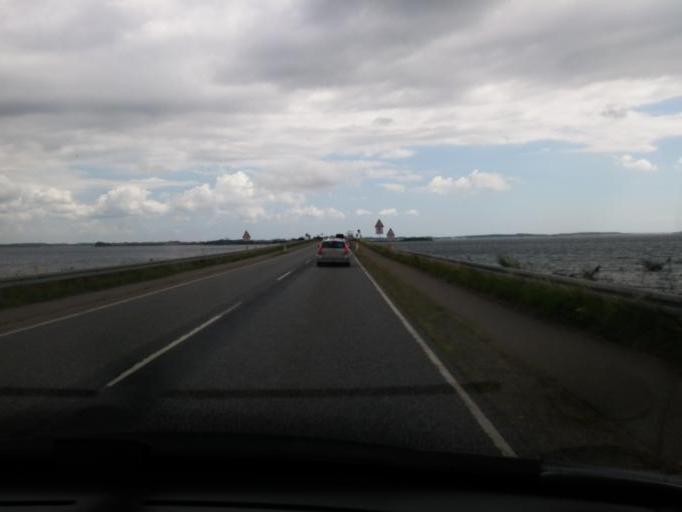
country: DK
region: South Denmark
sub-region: Langeland Kommune
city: Rudkobing
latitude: 54.9669
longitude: 10.6536
